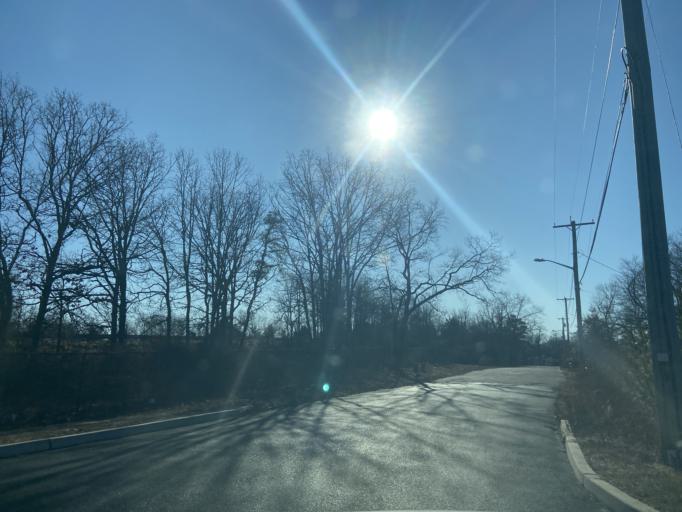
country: US
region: New Jersey
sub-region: Cumberland County
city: Vineland
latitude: 39.4974
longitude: -75.0707
